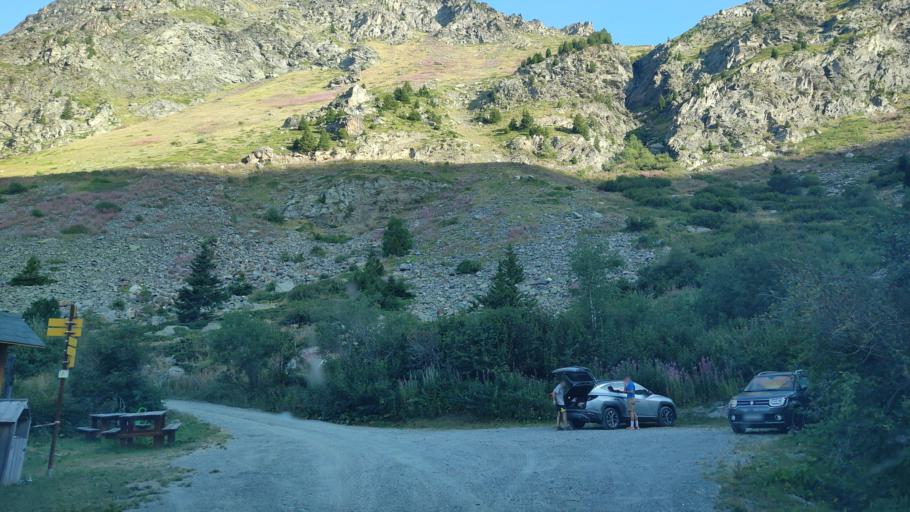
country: FR
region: Rhone-Alpes
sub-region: Departement de la Savoie
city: Val Thorens
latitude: 45.2368
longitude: 6.5584
